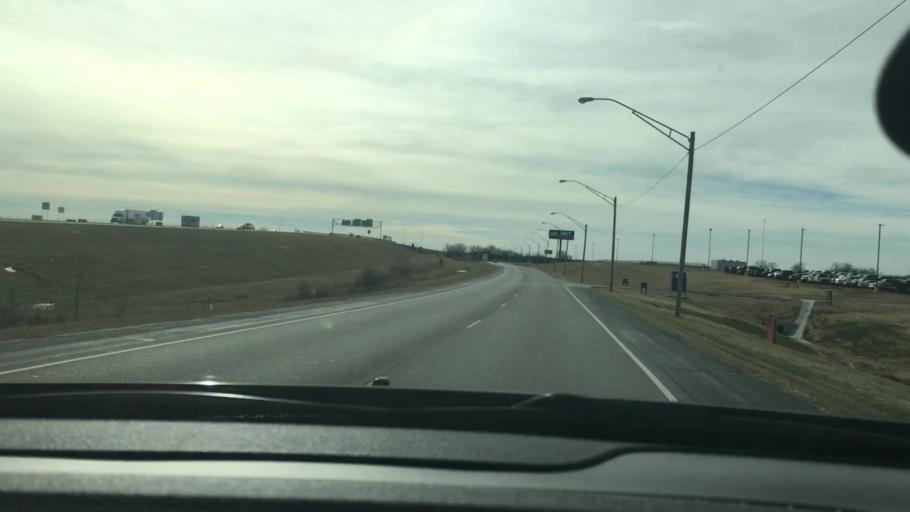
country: US
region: Oklahoma
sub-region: Carter County
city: Ardmore
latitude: 34.1813
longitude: -97.1689
